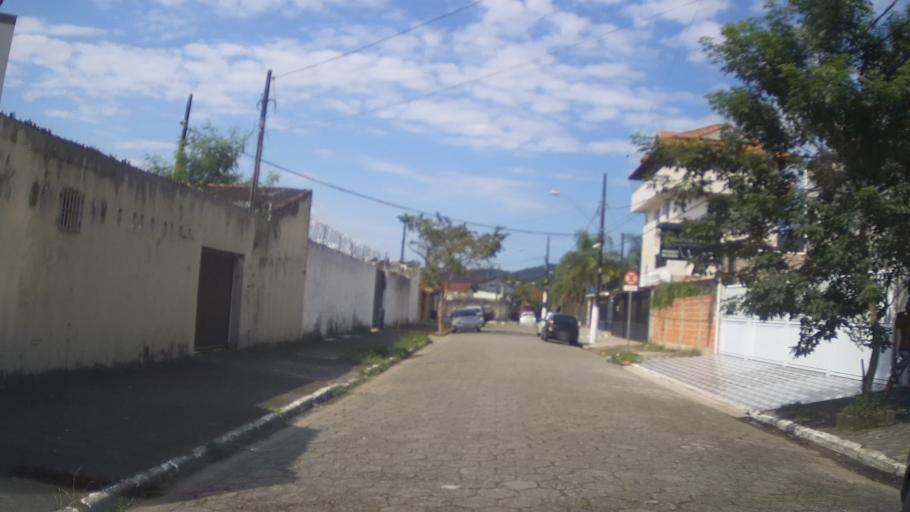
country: BR
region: Sao Paulo
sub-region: Praia Grande
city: Praia Grande
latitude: -24.0019
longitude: -46.4213
